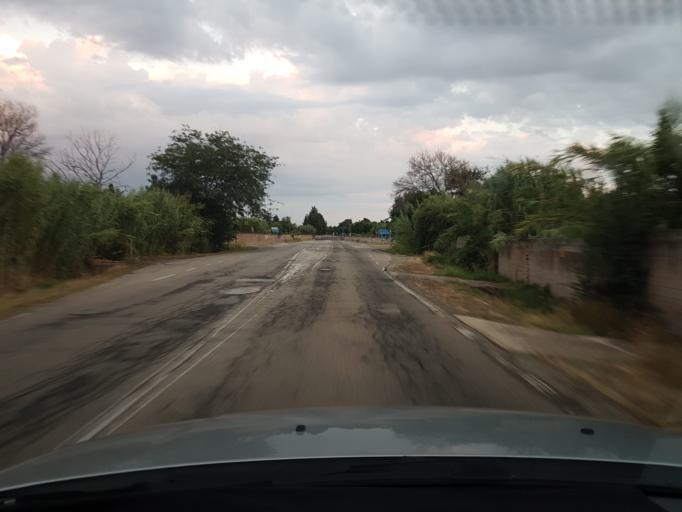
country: IT
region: Sardinia
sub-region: Provincia di Oristano
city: Milis
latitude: 40.0466
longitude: 8.6310
